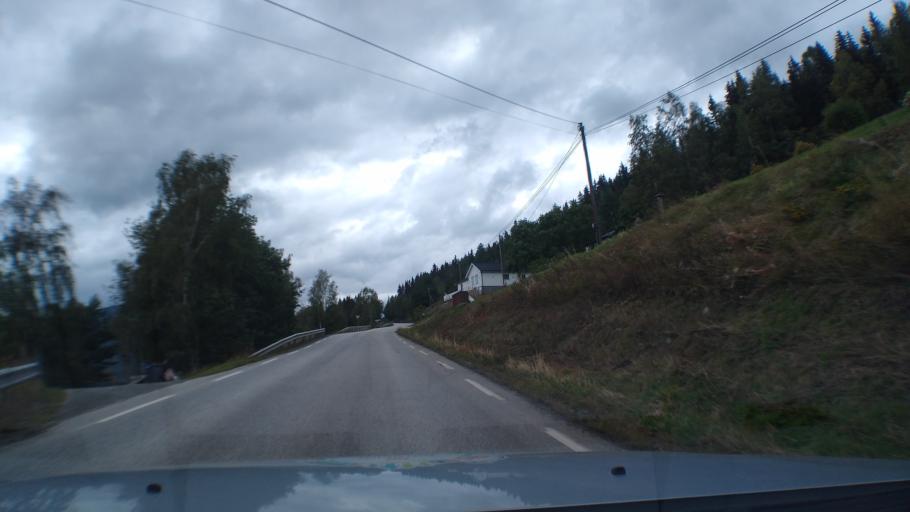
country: NO
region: Oppland
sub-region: Ringebu
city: Ringebu
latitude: 61.5539
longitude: 10.0853
